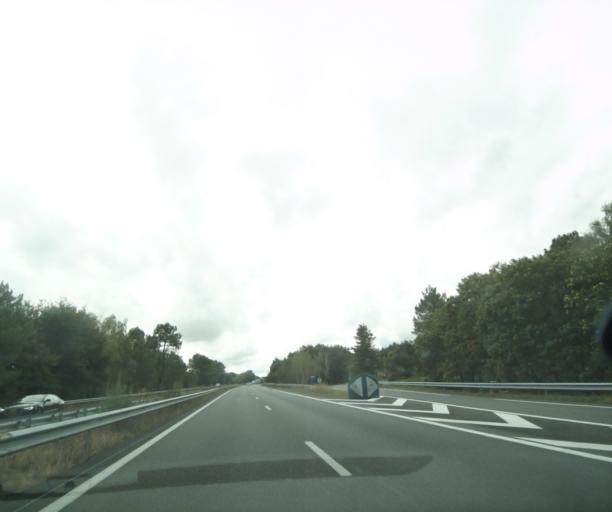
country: FR
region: Poitou-Charentes
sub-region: Departement de la Charente-Maritime
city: Saint-Genis-de-Saintonge
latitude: 45.4432
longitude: -0.6084
